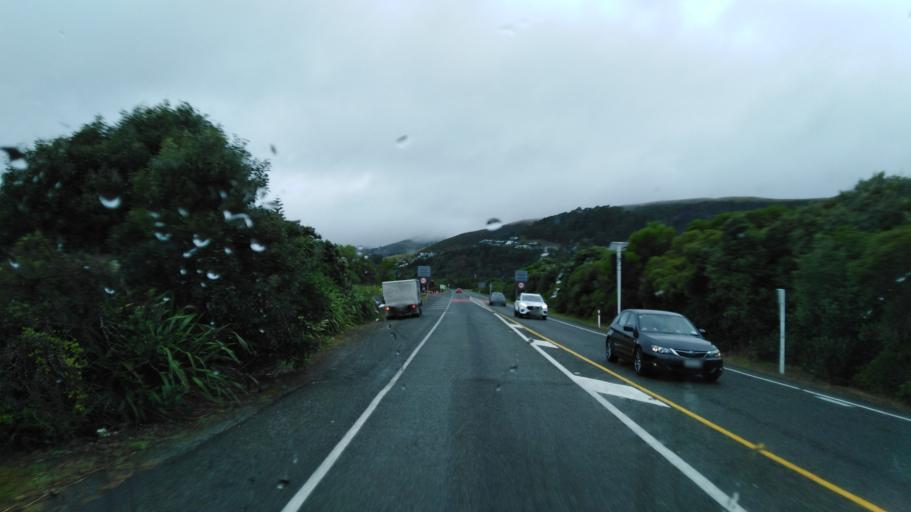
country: NZ
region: Nelson
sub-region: Nelson City
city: Nelson
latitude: -41.2645
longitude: 173.2858
